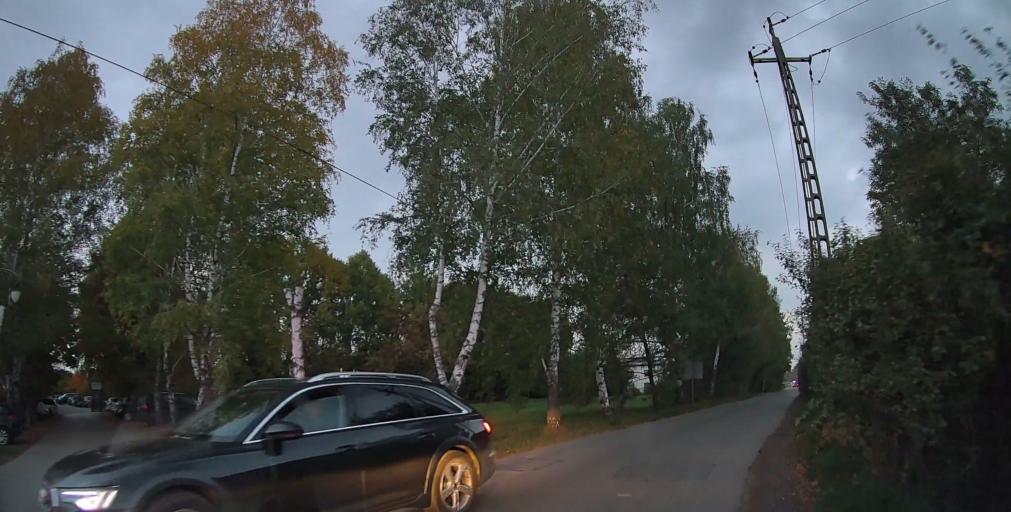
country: PL
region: Masovian Voivodeship
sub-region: Powiat piaseczynski
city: Mysiadlo
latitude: 52.1428
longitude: 21.0064
